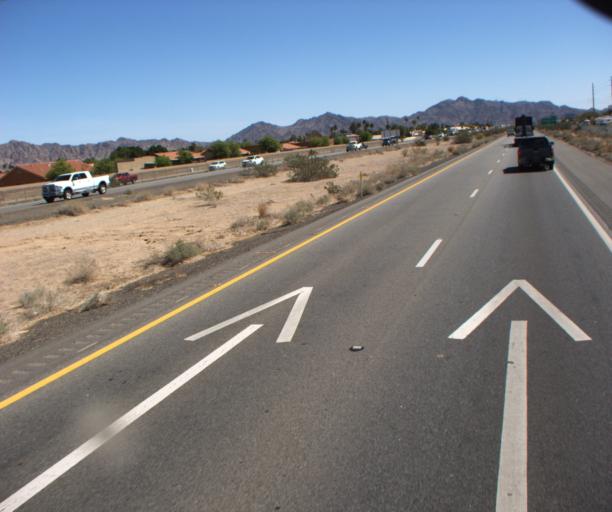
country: US
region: Arizona
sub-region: Yuma County
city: Fortuna Foothills
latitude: 32.6703
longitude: -114.4343
